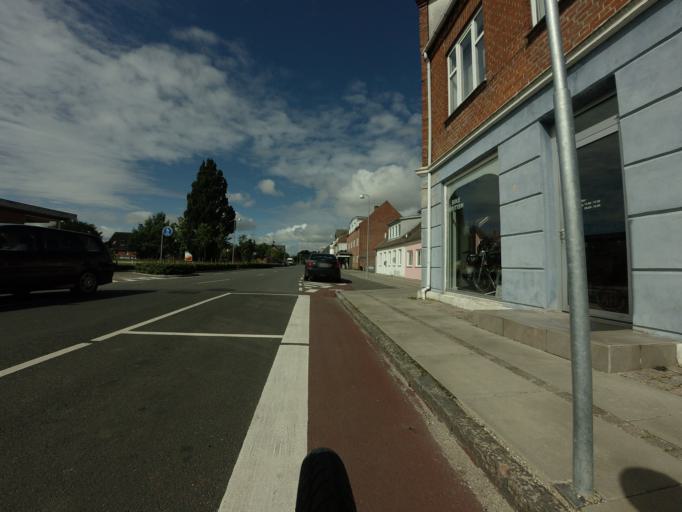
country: DK
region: Central Jutland
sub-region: Norddjurs Kommune
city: Allingabro
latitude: 56.4640
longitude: 10.3229
